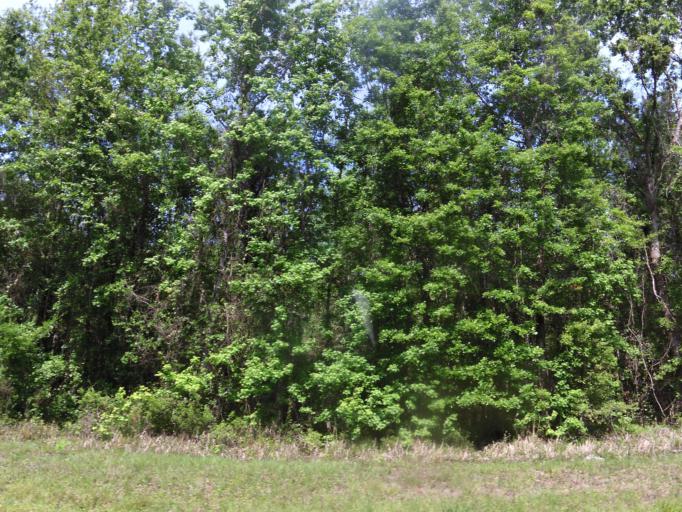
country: US
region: Georgia
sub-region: Camden County
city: Kingsland
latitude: 30.7998
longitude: -81.7229
